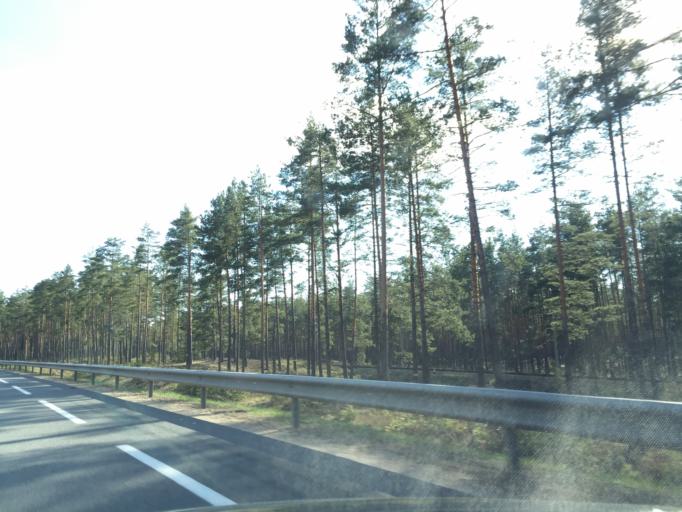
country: LV
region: Saulkrastu
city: Saulkrasti
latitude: 57.2858
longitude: 24.4335
